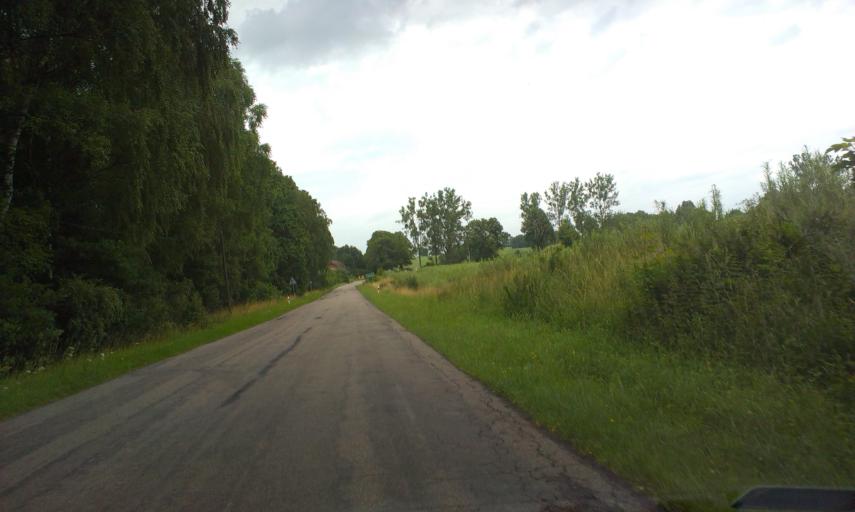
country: PL
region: West Pomeranian Voivodeship
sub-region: Powiat szczecinecki
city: Barwice
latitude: 53.6818
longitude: 16.3407
